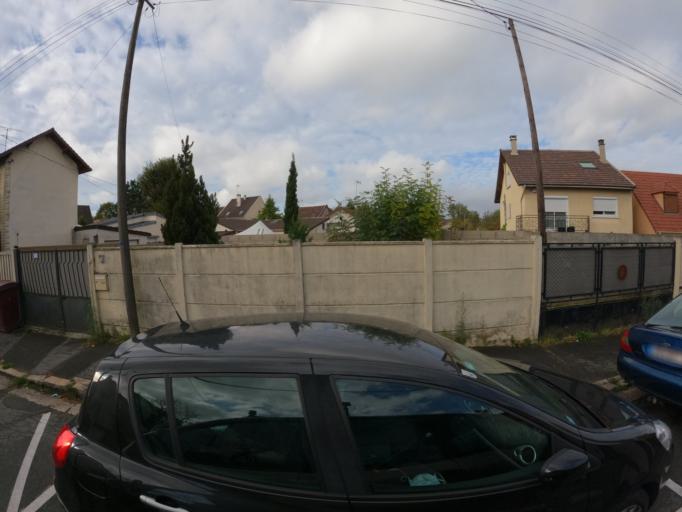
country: FR
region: Ile-de-France
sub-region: Departement de Seine-Saint-Denis
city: Montfermeil
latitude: 48.9024
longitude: 2.5882
